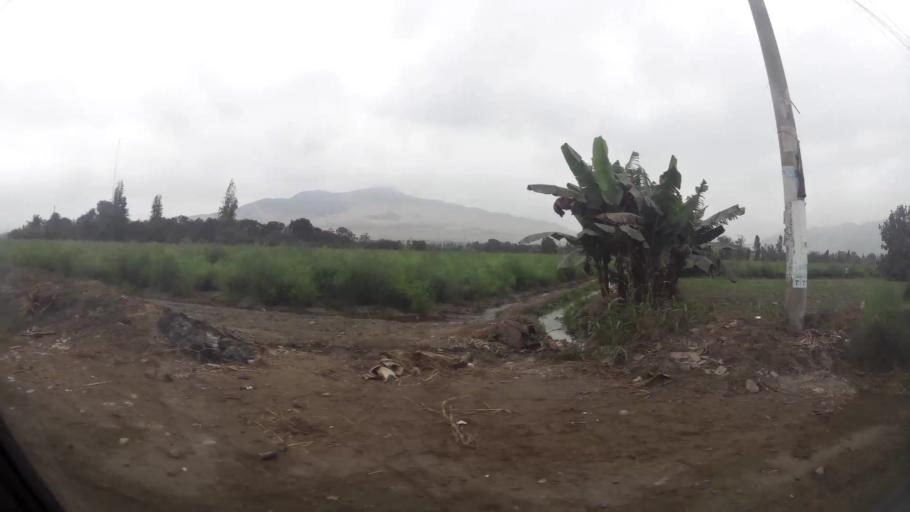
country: PE
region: Lima
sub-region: Provincia de Huaral
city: Huaral
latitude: -11.5253
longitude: -77.2472
